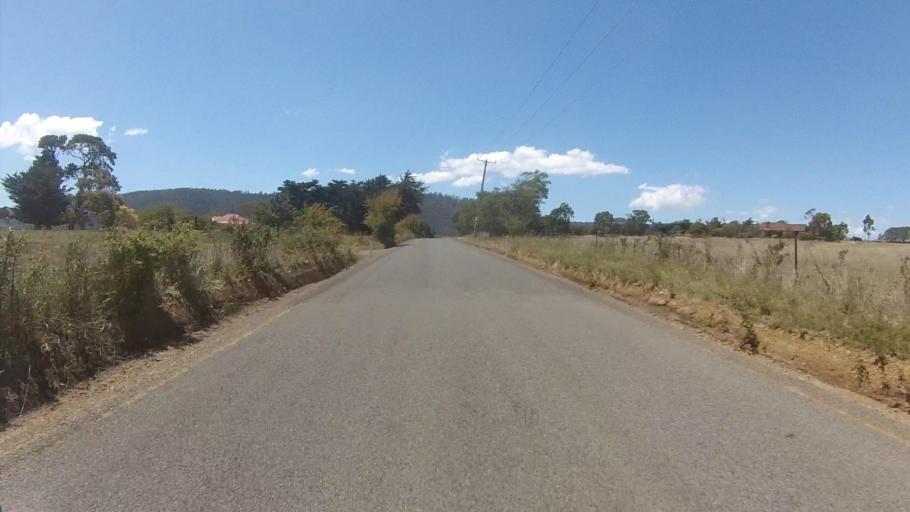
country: AU
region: Tasmania
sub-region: Sorell
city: Sorell
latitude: -42.7615
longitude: 147.6196
